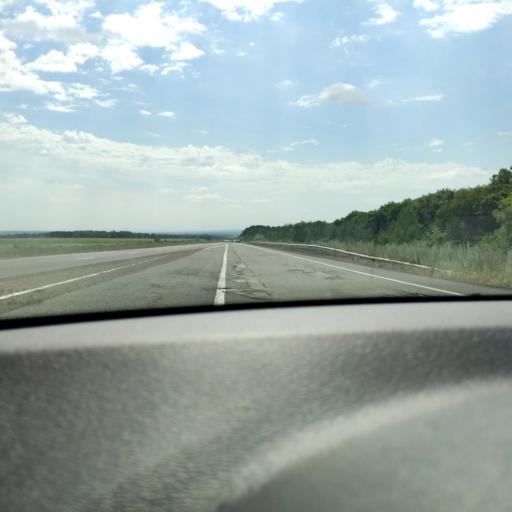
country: RU
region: Samara
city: Petra-Dubrava
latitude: 53.3306
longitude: 50.4285
